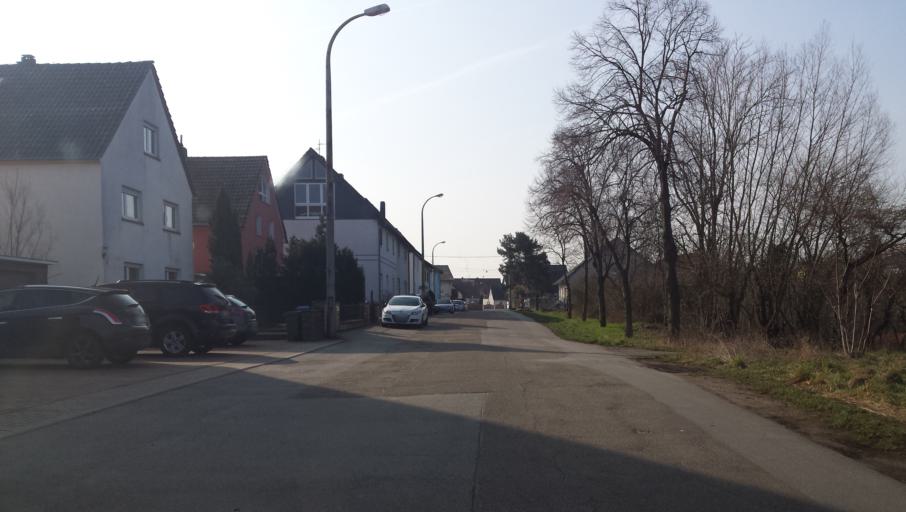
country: DE
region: Hesse
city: Lampertheim
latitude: 49.5637
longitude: 8.4485
